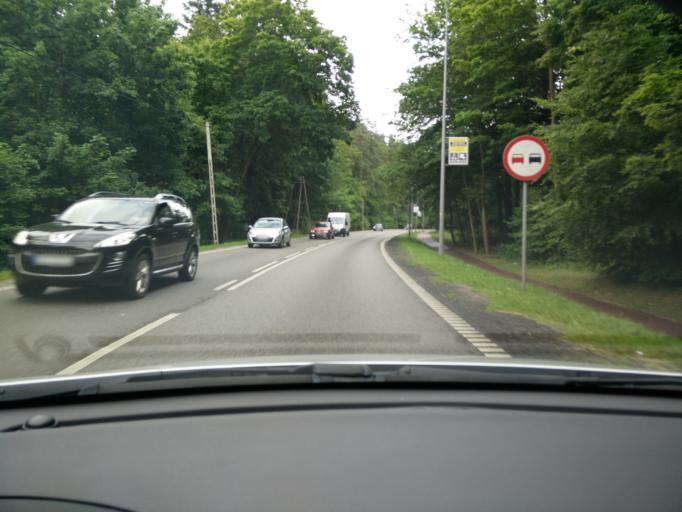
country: PL
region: Pomeranian Voivodeship
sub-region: Sopot
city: Sopot
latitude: 54.4156
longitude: 18.5455
